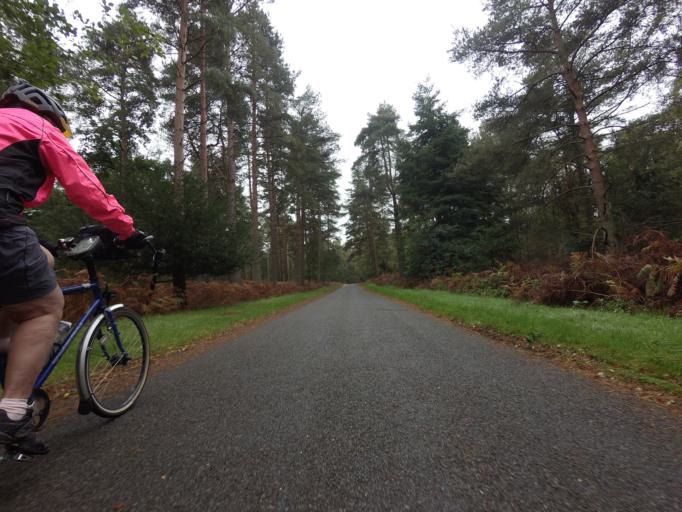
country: GB
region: England
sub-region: Norfolk
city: Dersingham
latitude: 52.8177
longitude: 0.4924
